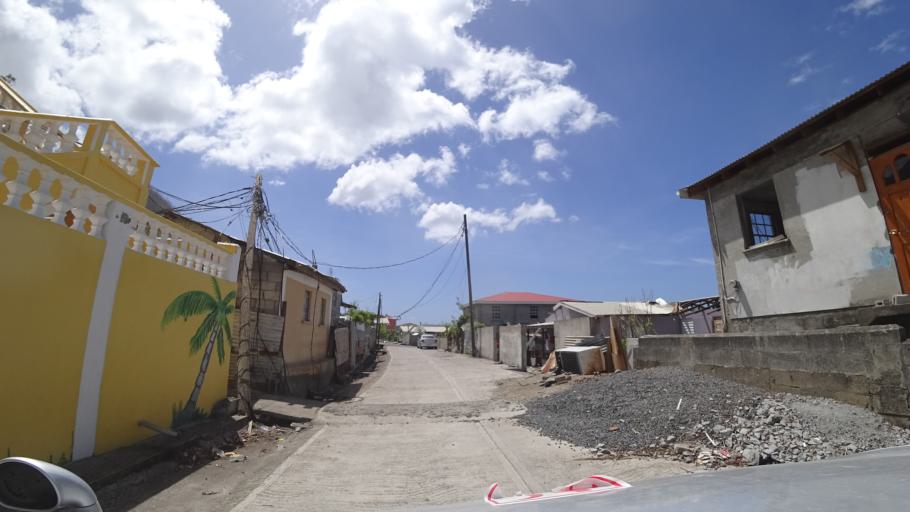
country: DM
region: Saint Luke
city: Pointe Michel
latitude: 15.2621
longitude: -61.3766
